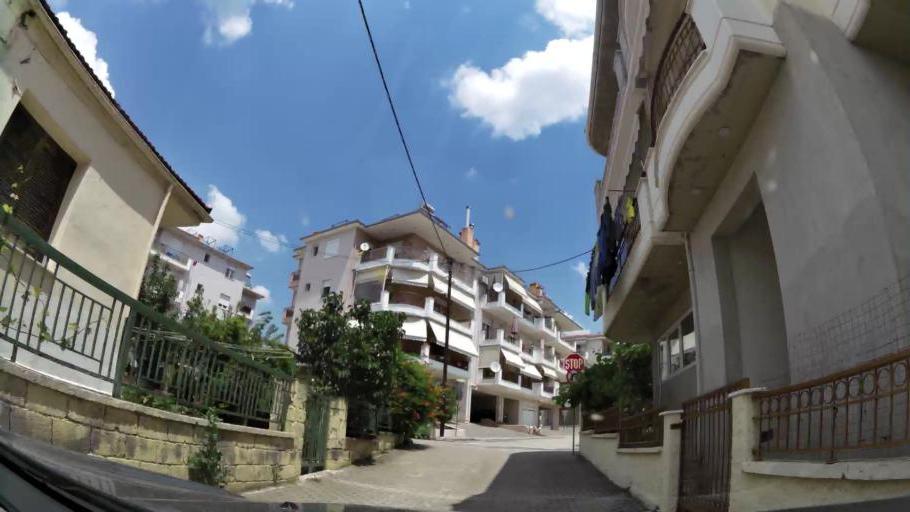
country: GR
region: West Macedonia
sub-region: Nomos Kozanis
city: Kozani
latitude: 40.2928
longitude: 21.7972
